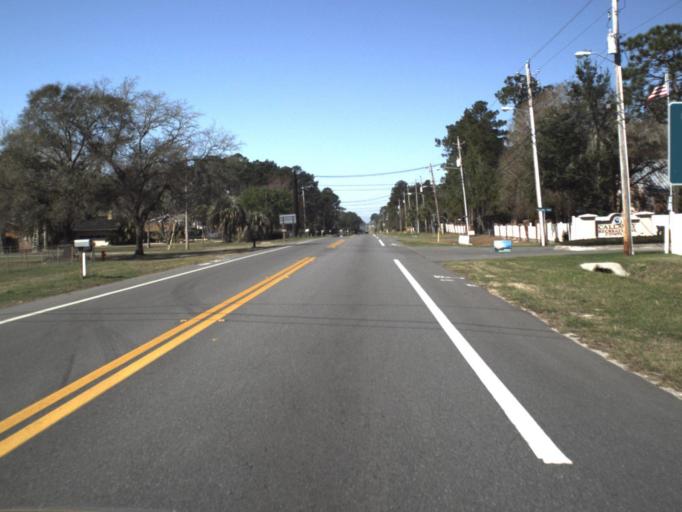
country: US
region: Florida
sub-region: Bay County
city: Callaway
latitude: 30.1528
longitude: -85.5460
